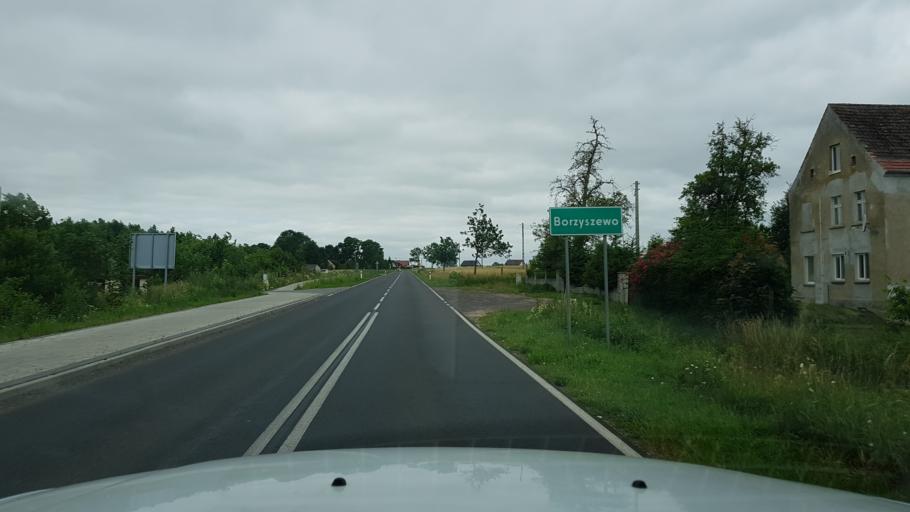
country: PL
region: West Pomeranian Voivodeship
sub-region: Powiat gryficki
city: Gryfice
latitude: 53.9073
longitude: 15.1837
